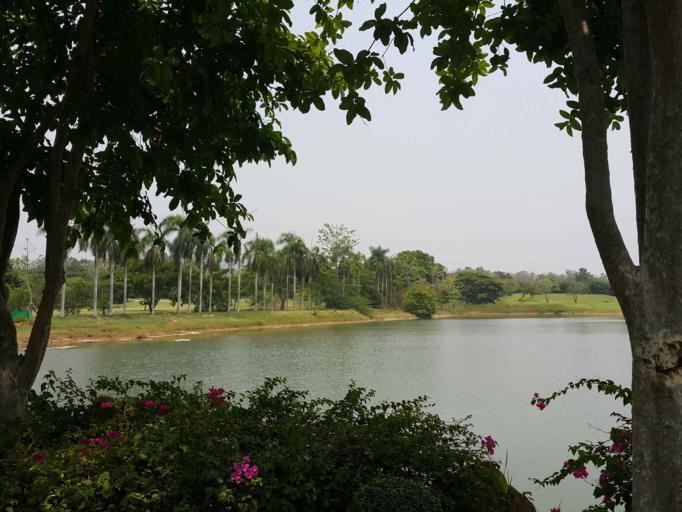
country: TH
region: Chiang Mai
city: San Sai
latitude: 18.9134
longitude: 99.0383
